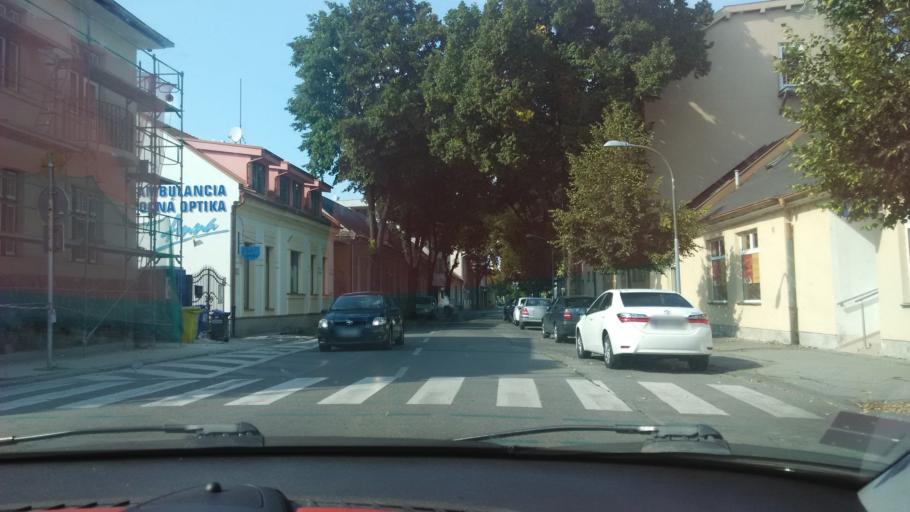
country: SK
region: Trnavsky
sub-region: Okres Trnava
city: Piestany
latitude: 48.5935
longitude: 17.8336
